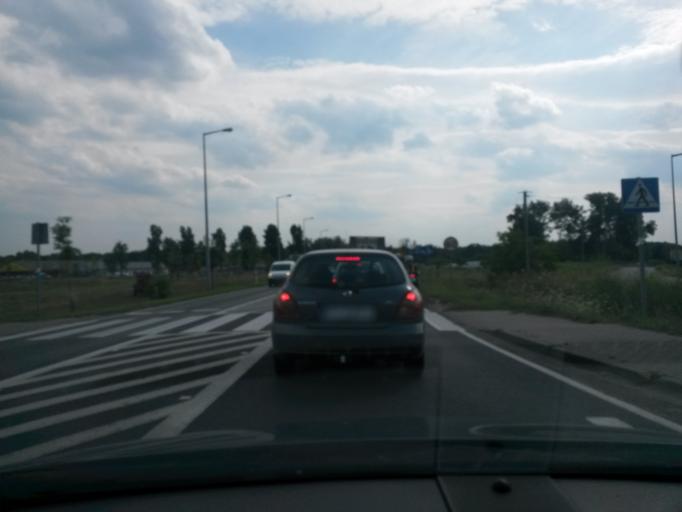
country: PL
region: Greater Poland Voivodeship
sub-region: Powiat poznanski
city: Kornik
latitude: 52.2563
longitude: 17.0789
